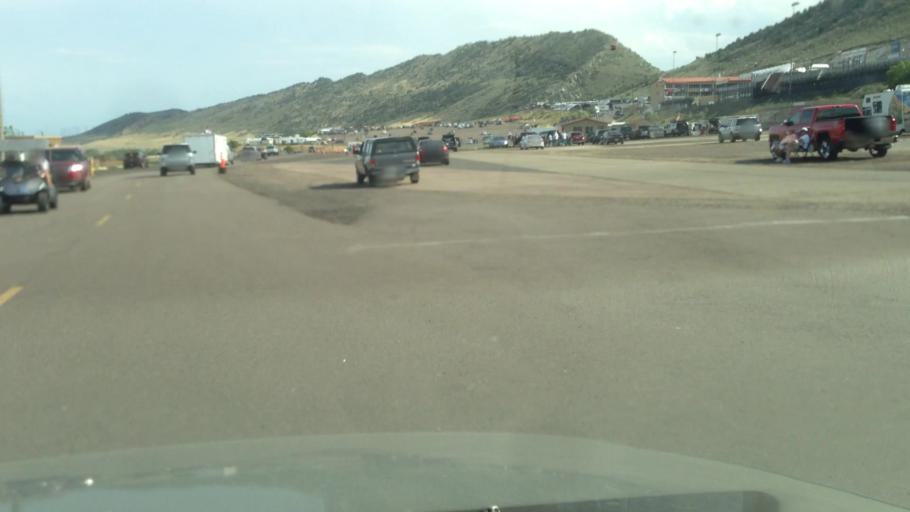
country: US
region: Colorado
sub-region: Jefferson County
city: Indian Hills
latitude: 39.6636
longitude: -105.1864
